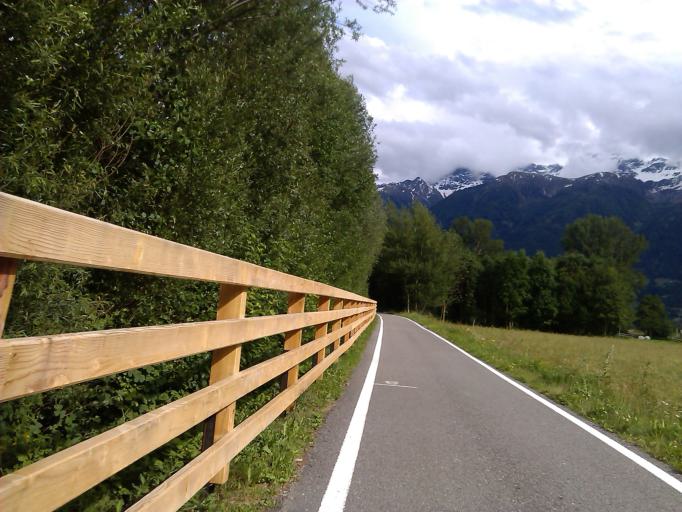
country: IT
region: Trentino-Alto Adige
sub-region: Bolzano
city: Sluderno
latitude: 46.6474
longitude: 10.5771
